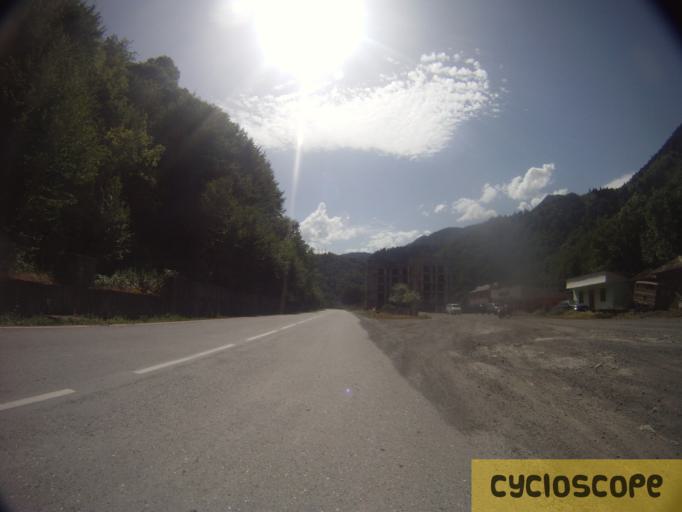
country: GE
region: Samegrelo and Zemo Svaneti
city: Jvari
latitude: 42.9448
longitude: 42.1872
